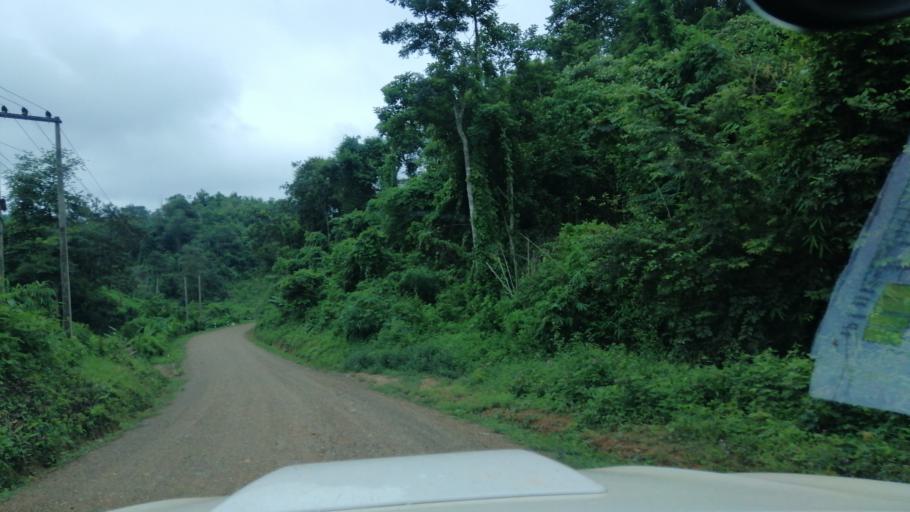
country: LA
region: Xiagnabouli
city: Muang Kenthao
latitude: 17.9299
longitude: 101.3854
